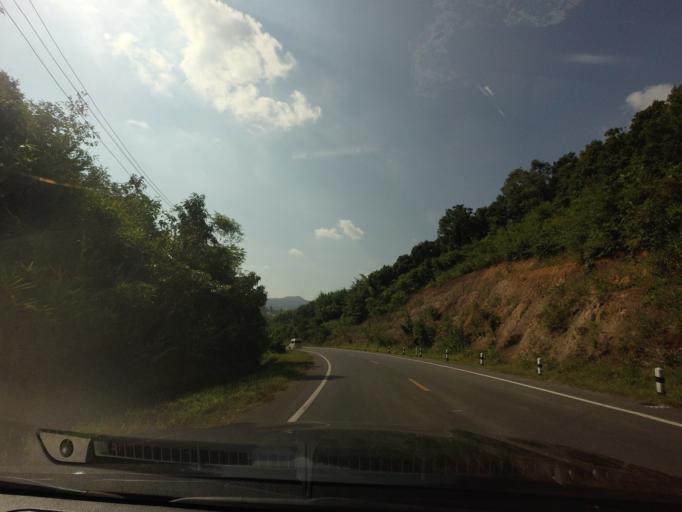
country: TH
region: Nan
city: Santi Suk
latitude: 18.9248
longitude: 100.9070
